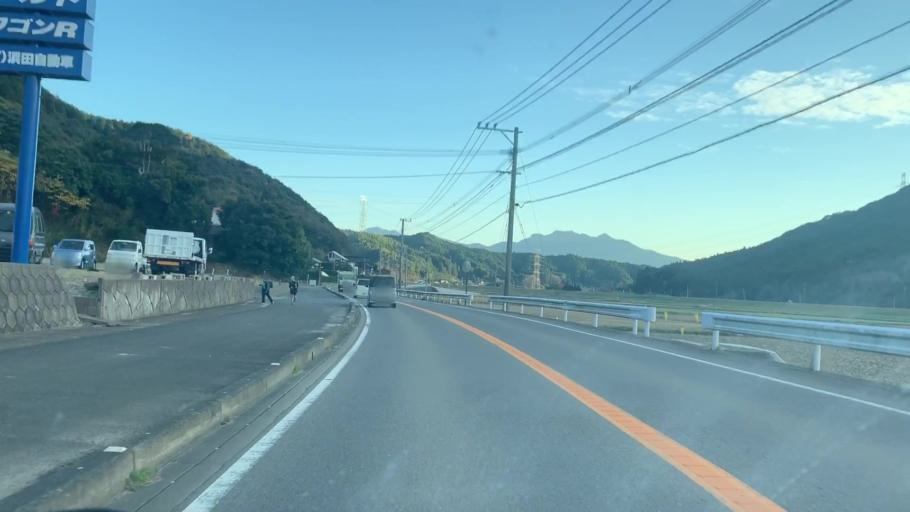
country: JP
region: Saga Prefecture
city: Karatsu
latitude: 33.3691
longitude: 130.0042
